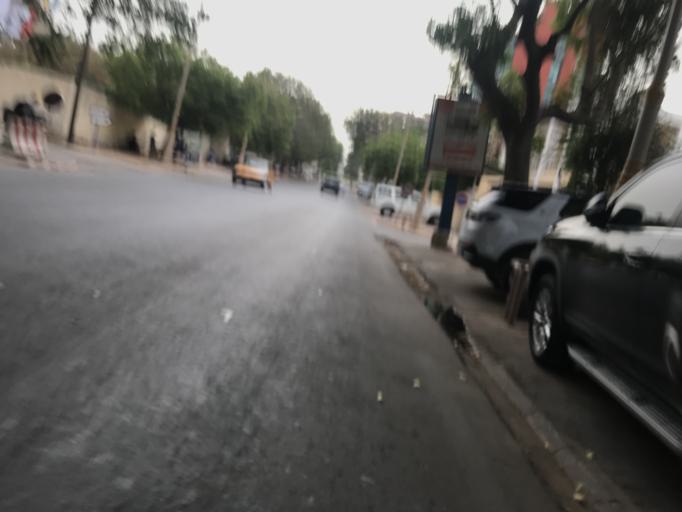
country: SN
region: Dakar
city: Dakar
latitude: 14.6627
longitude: -17.4357
